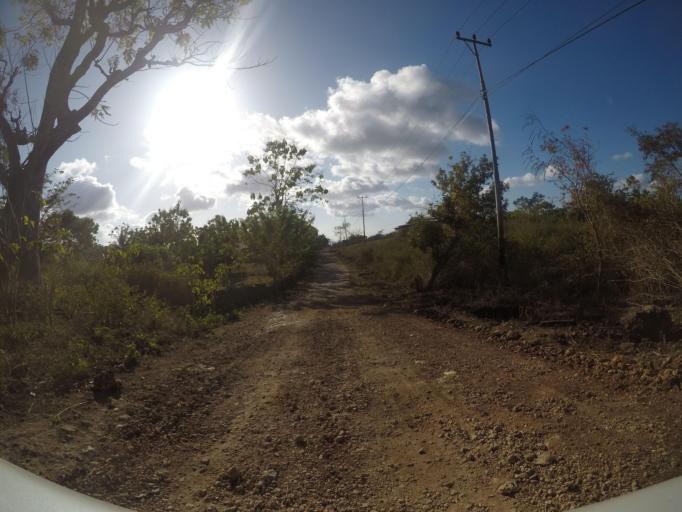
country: TL
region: Lautem
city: Lospalos
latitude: -8.4418
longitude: 126.8633
